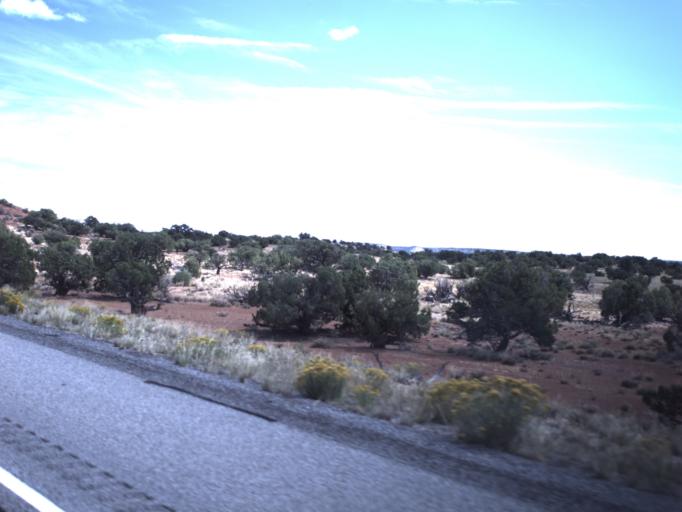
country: US
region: Utah
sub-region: Emery County
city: Castle Dale
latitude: 38.8670
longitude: -110.7134
